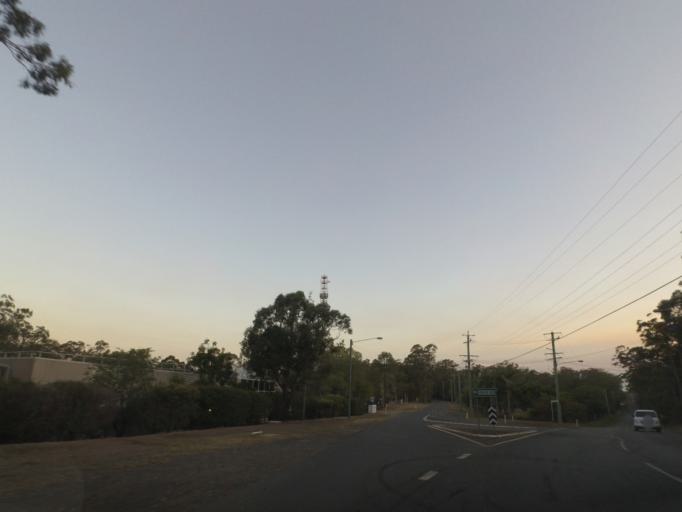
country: AU
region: Queensland
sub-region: Brisbane
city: Mackenzie
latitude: -27.5529
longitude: 153.1302
